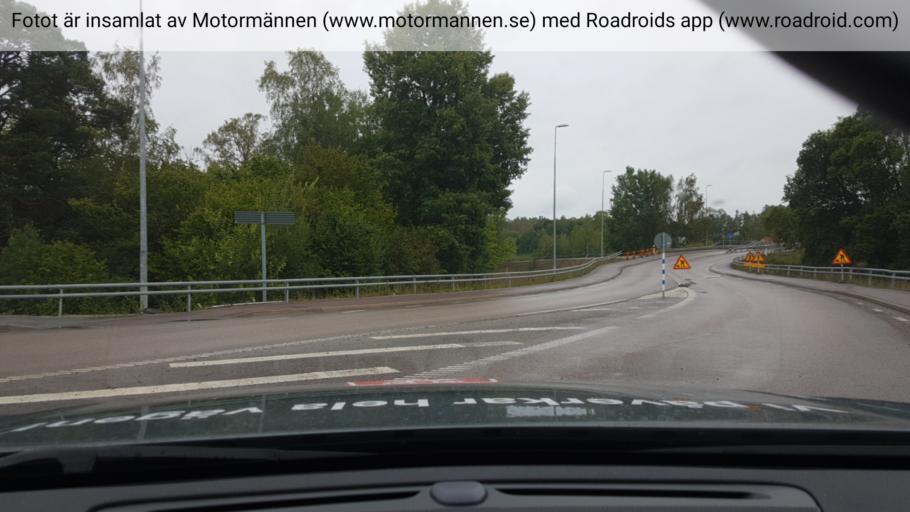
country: SE
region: Stockholm
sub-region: Nynashamns Kommun
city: Osmo
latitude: 58.9431
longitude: 17.9131
